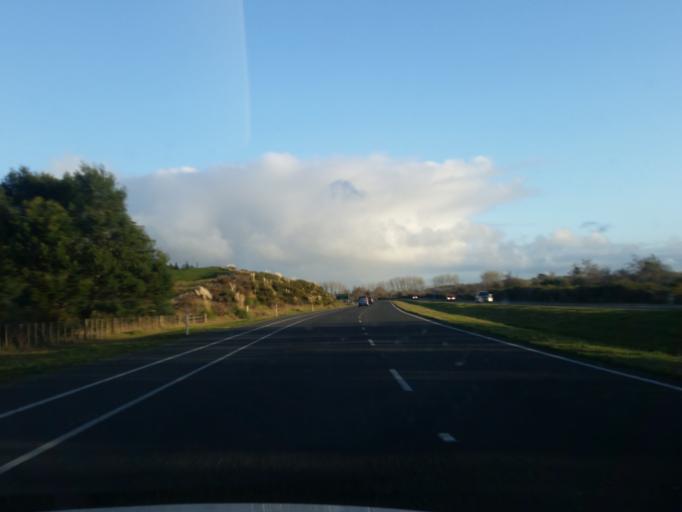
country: NZ
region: Waikato
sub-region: Waikato District
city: Te Kauwhata
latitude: -37.3287
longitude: 175.0652
